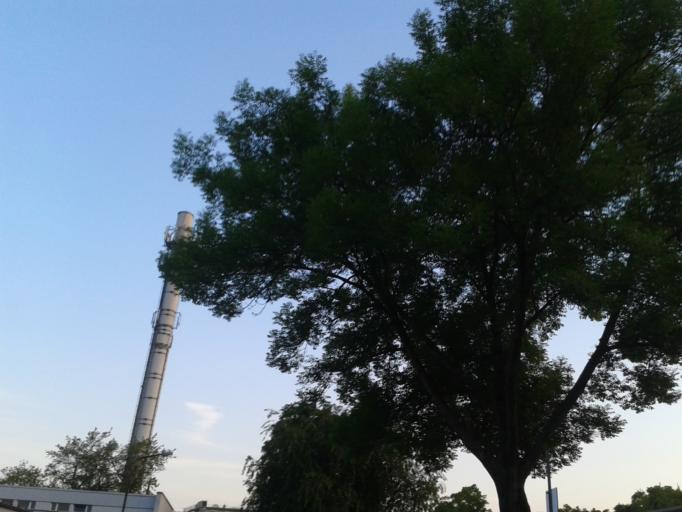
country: DE
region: Saxony
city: Dresden
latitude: 51.0674
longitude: 13.7458
